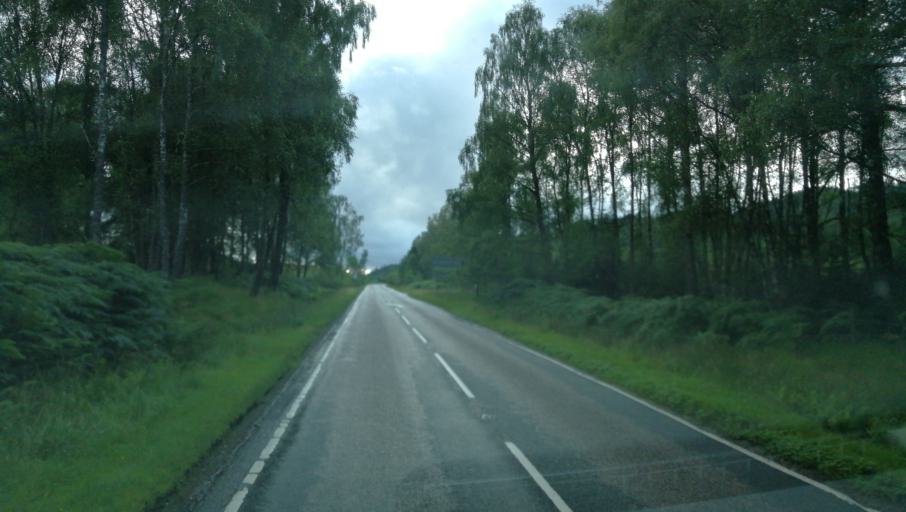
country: GB
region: Scotland
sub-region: Highland
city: Spean Bridge
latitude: 57.0834
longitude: -4.9025
